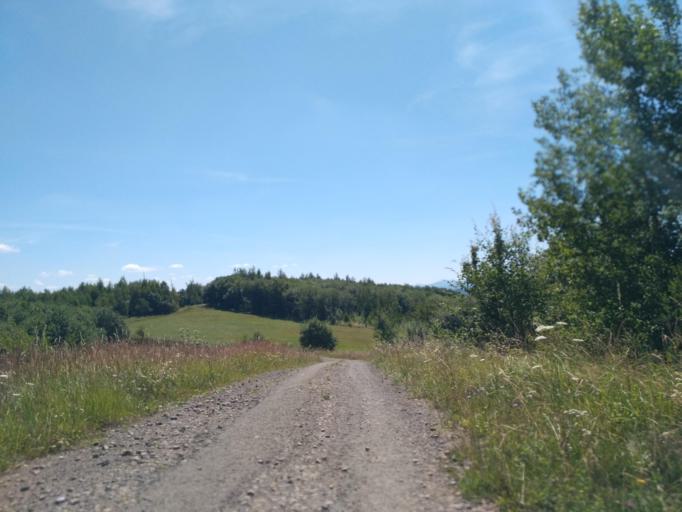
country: PL
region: Subcarpathian Voivodeship
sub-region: Powiat sanocki
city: Bukowsko
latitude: 49.5048
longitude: 22.0579
